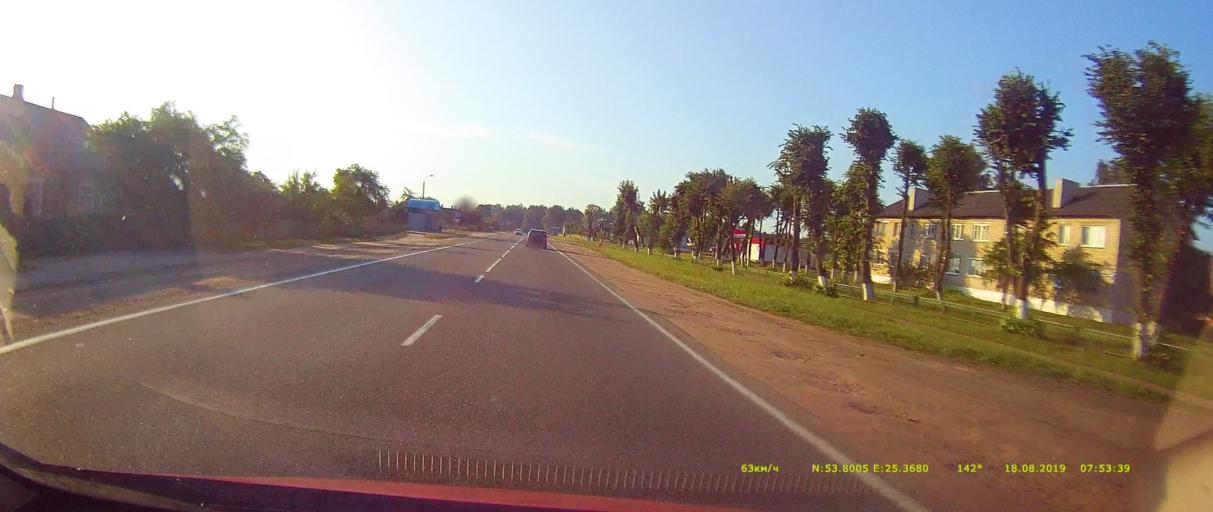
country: BY
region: Grodnenskaya
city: Dzyatlava
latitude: 53.4699
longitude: 25.4020
